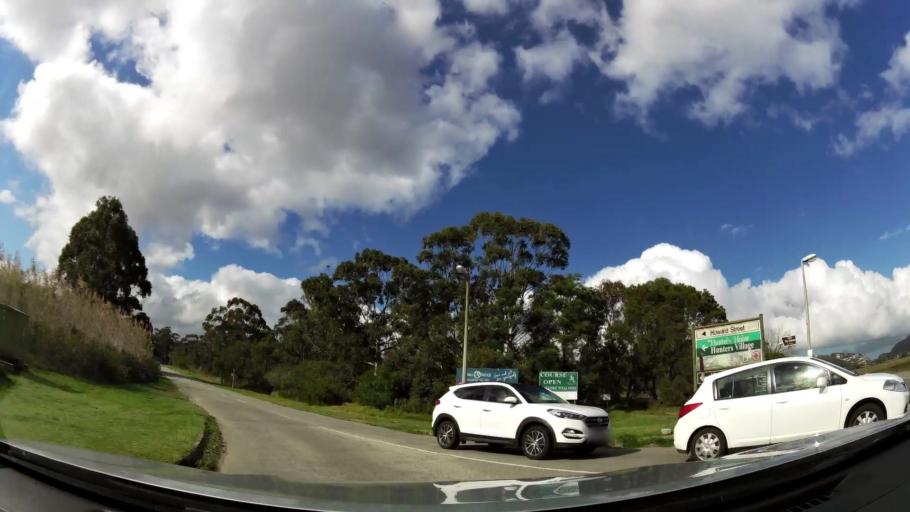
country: ZA
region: Western Cape
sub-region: Eden District Municipality
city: Knysna
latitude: -34.0533
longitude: 23.0699
